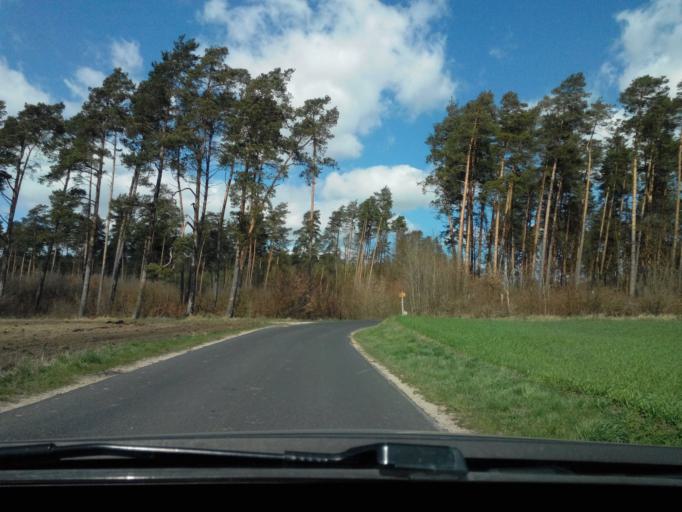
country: PL
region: Warmian-Masurian Voivodeship
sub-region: Powiat nowomiejski
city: Biskupiec
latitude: 53.4490
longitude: 19.3273
